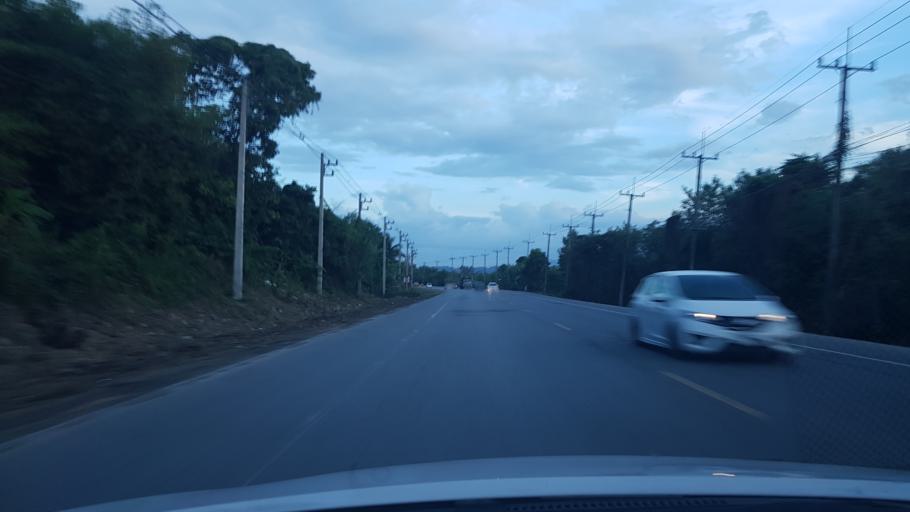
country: TH
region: Sara Buri
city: Kaeng Khoi
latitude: 14.4806
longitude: 101.0532
